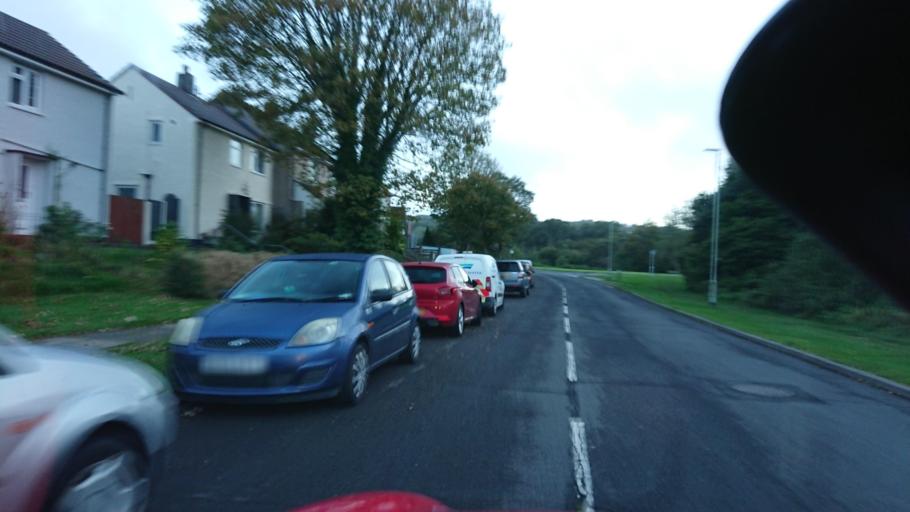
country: GB
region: England
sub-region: Cornwall
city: Saltash
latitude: 50.4205
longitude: -4.1836
